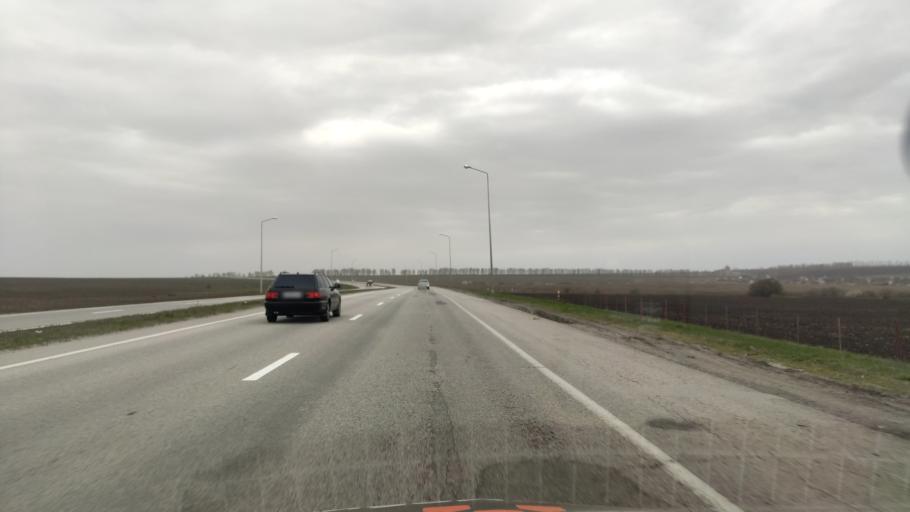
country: RU
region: Belgorod
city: Staryy Oskol
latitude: 51.3391
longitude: 37.7782
